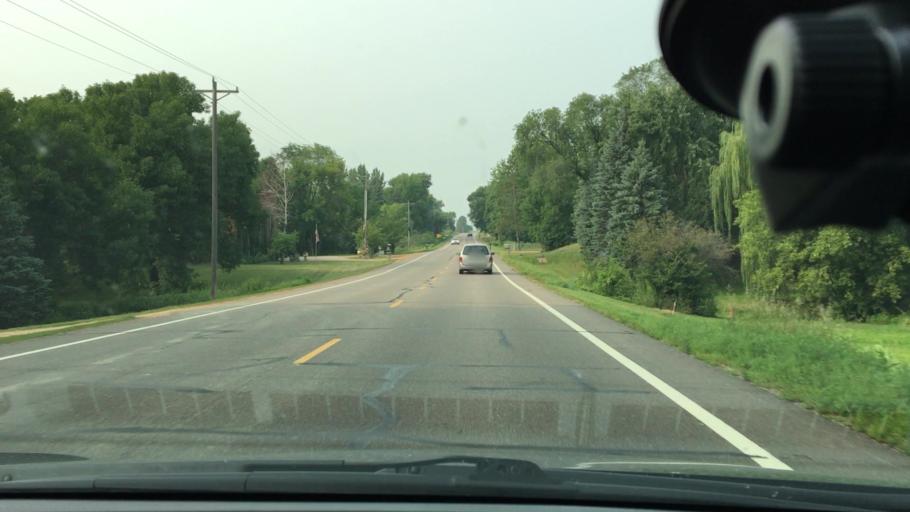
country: US
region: Minnesota
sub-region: Hennepin County
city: Champlin
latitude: 45.1691
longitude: -93.4621
